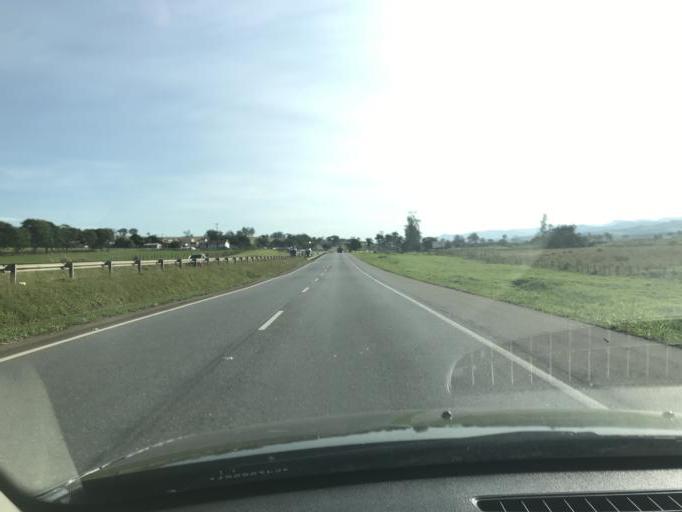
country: BR
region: Minas Gerais
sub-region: Santa Rita Do Sapucai
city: Santa Rita do Sapucai
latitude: -22.1210
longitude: -45.7669
